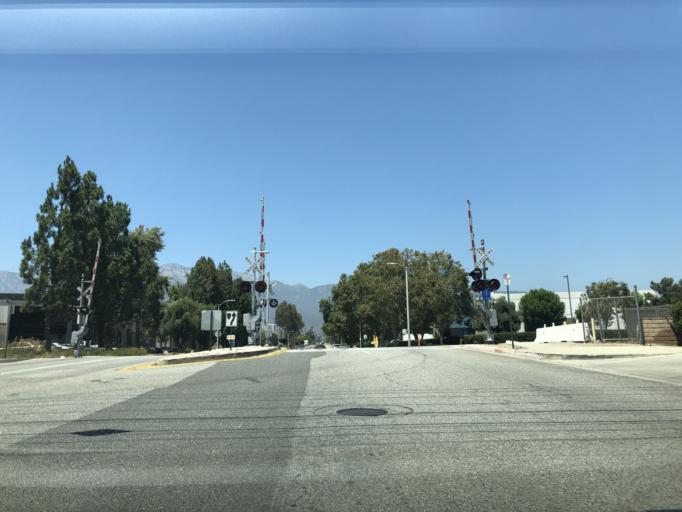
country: US
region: California
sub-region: San Bernardino County
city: Rancho Cucamonga
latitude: 34.0920
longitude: -117.5458
